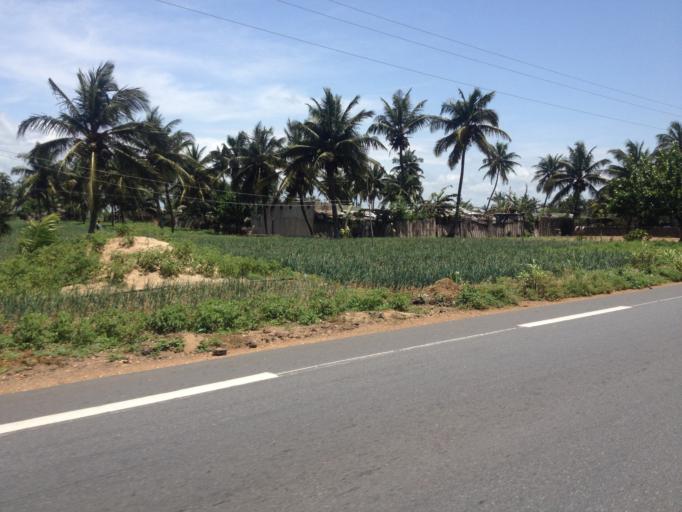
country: BJ
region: Mono
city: Grand-Popo
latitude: 6.2685
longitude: 1.7763
